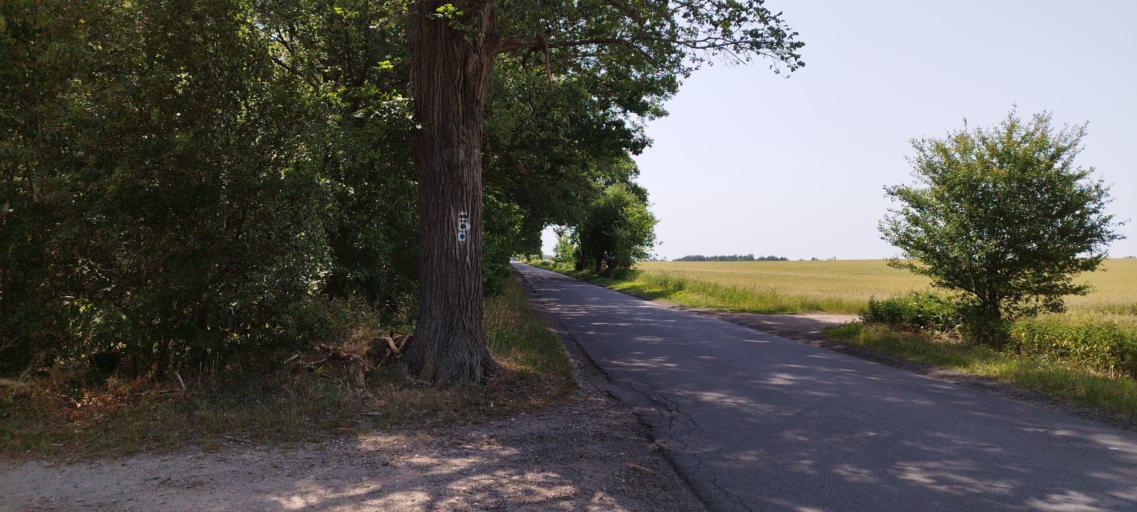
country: DE
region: Brandenburg
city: Rauen
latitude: 52.3338
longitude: 14.0443
